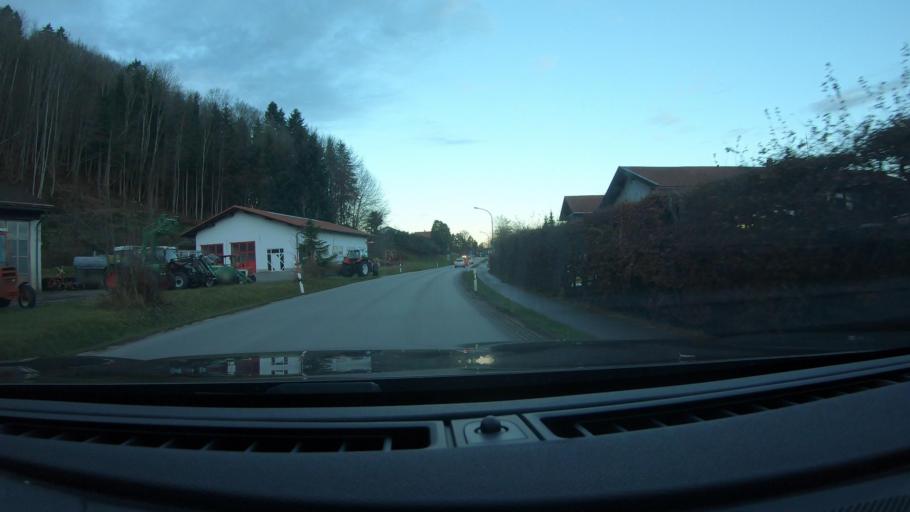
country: DE
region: Bavaria
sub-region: Upper Bavaria
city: Siegsdorf
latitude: 47.8246
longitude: 12.6382
